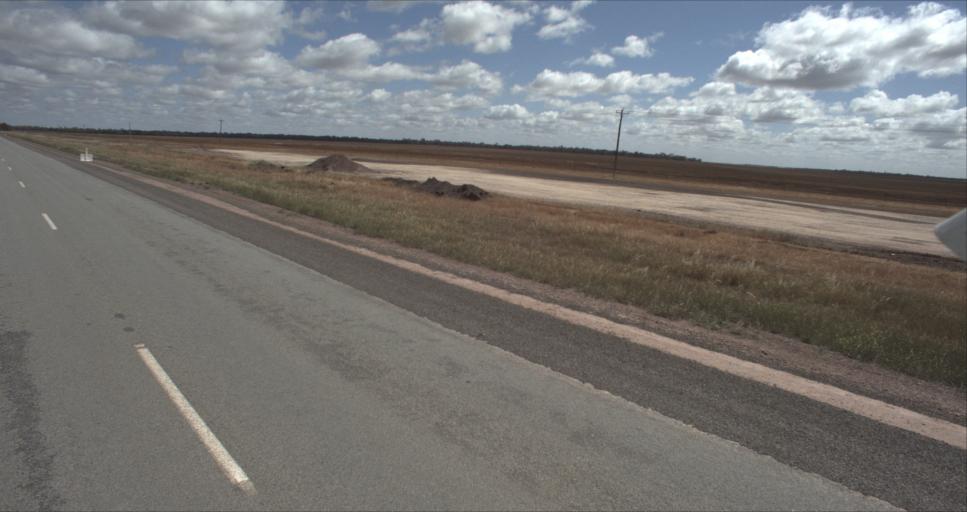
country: AU
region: New South Wales
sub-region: Murrumbidgee Shire
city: Darlington Point
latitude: -34.5717
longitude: 146.0379
